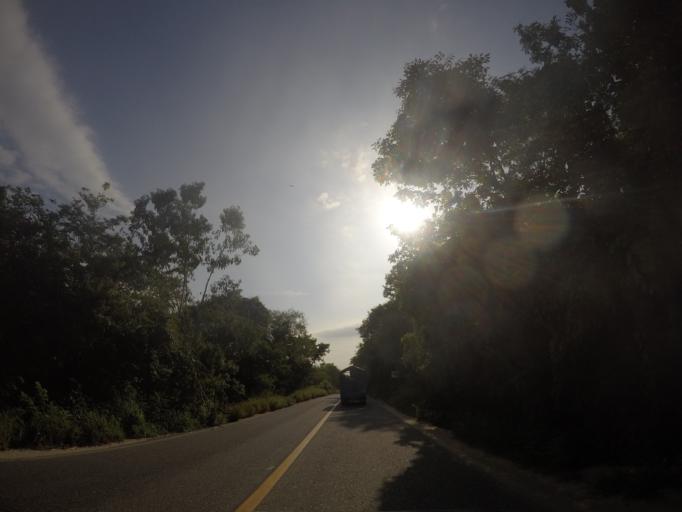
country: MX
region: Oaxaca
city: San Pedro Pochutla
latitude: 15.7322
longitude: -96.4981
